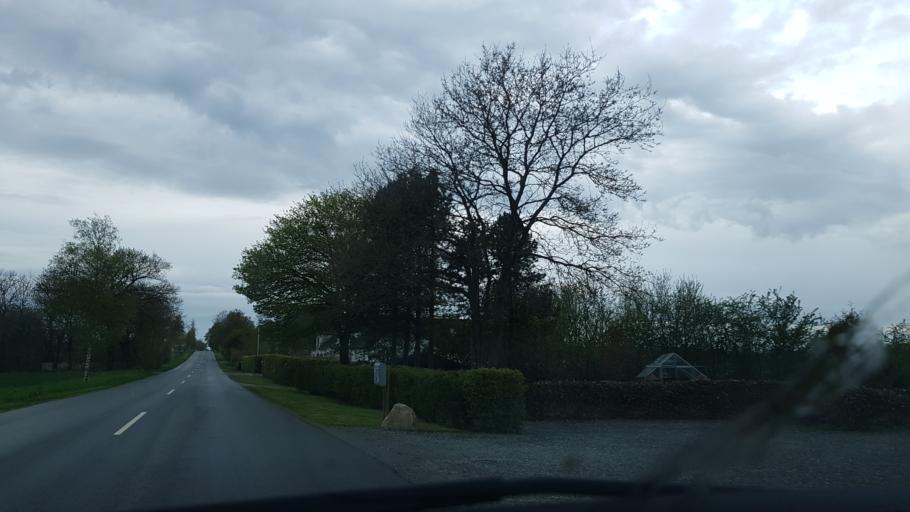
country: DK
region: South Denmark
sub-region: Kolding Kommune
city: Lunderskov
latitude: 55.4633
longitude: 9.3781
